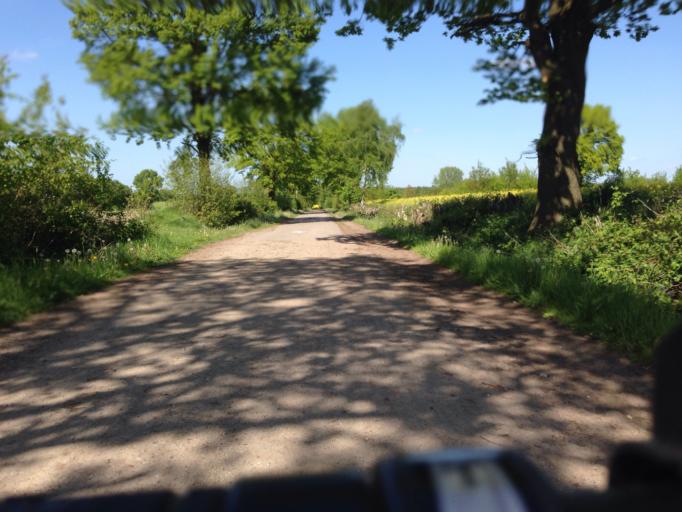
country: DE
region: Schleswig-Holstein
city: Stapelfeld
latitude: 53.5902
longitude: 10.2007
